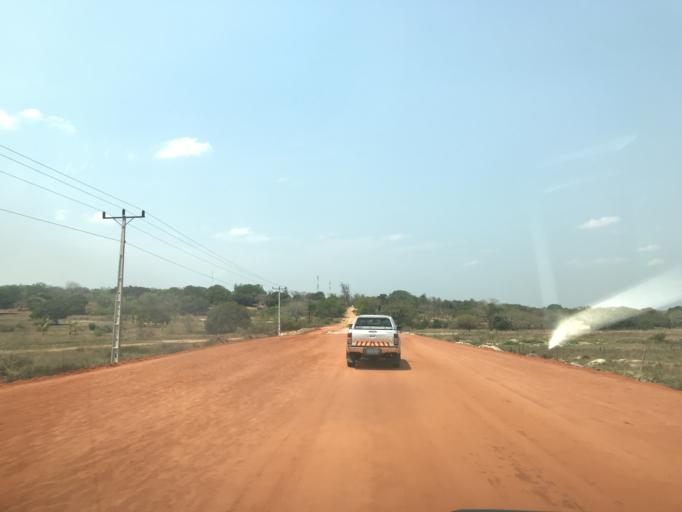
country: MZ
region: Gaza
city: Manjacaze
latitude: -24.4901
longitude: 33.9516
